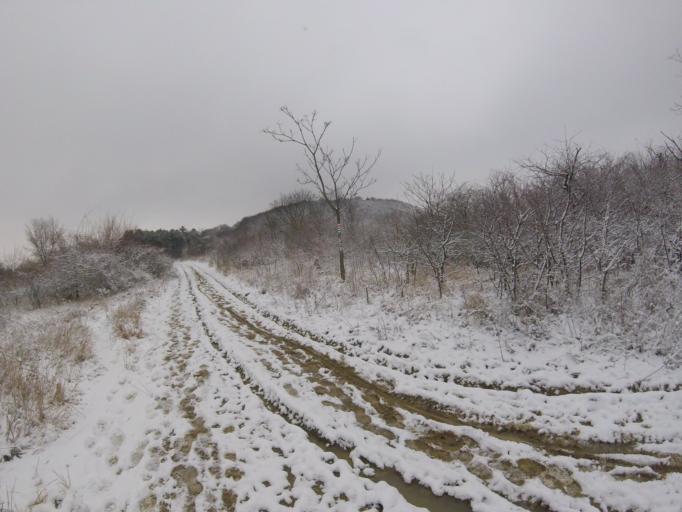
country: HU
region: Komarom-Esztergom
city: Esztergom
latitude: 47.7891
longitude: 18.7669
